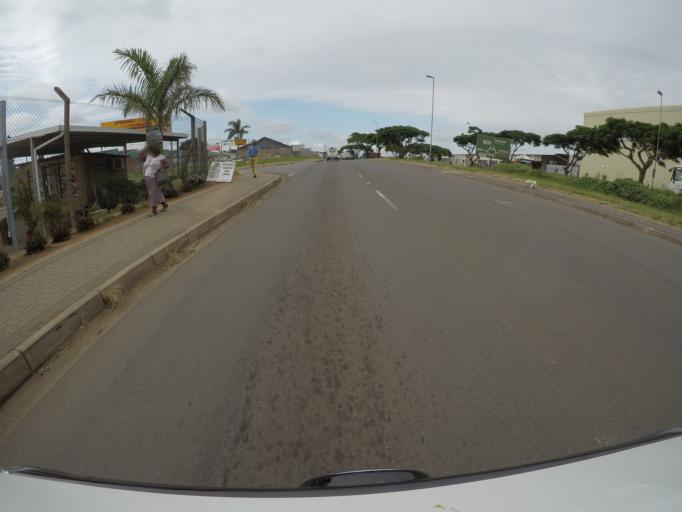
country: ZA
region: KwaZulu-Natal
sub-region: uThungulu District Municipality
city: Empangeni
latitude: -28.7761
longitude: 31.9006
